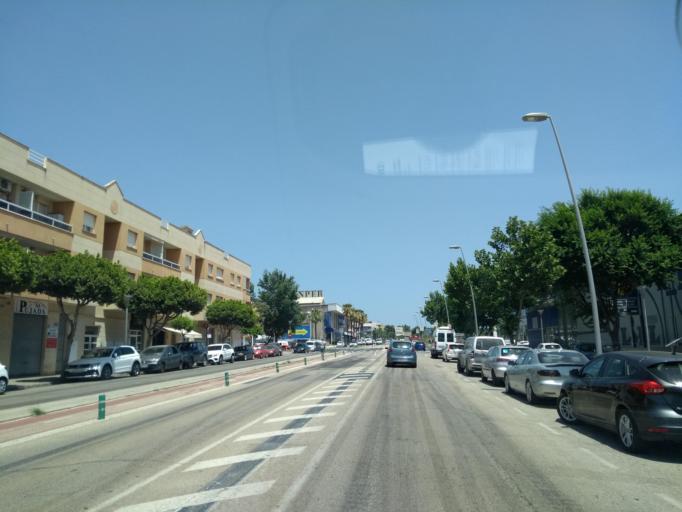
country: ES
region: Balearic Islands
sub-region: Illes Balears
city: Inca
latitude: 39.7219
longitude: 2.9186
